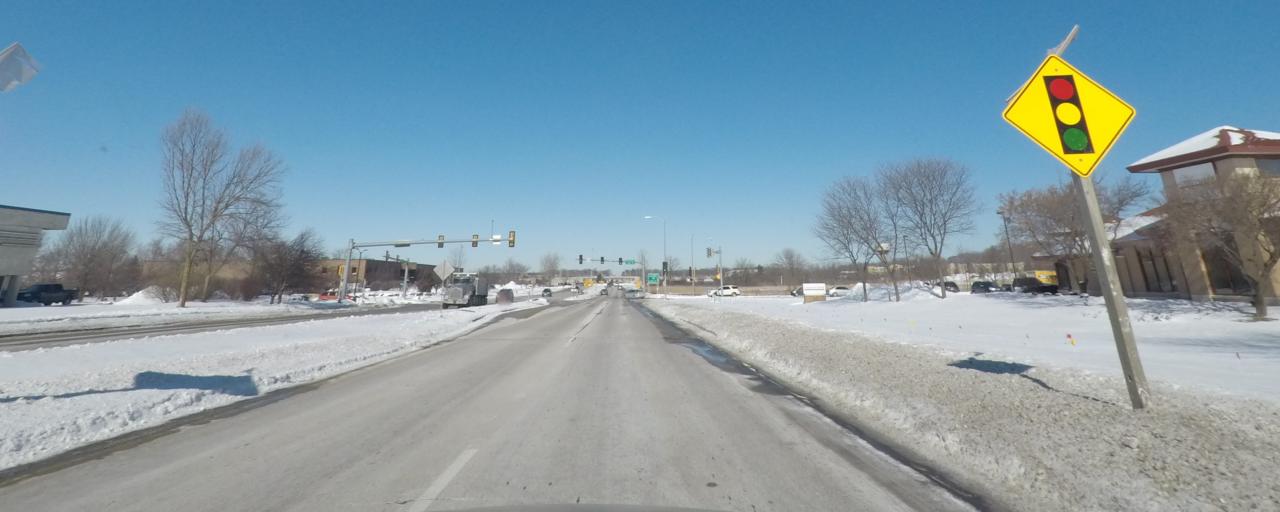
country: US
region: Wisconsin
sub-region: Waukesha County
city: New Berlin
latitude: 42.9457
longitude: -88.1090
